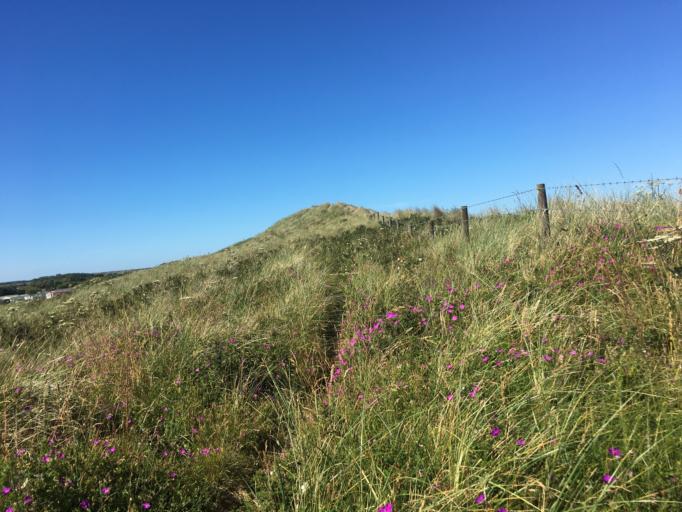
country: GB
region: England
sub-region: Northumberland
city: Beadnell
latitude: 55.5436
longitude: -1.6367
